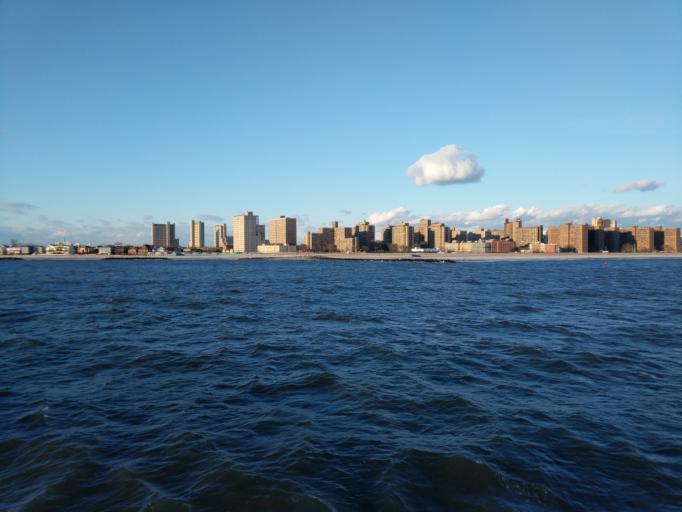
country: US
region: New York
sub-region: Kings County
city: Coney Island
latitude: 40.5675
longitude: -74.0045
